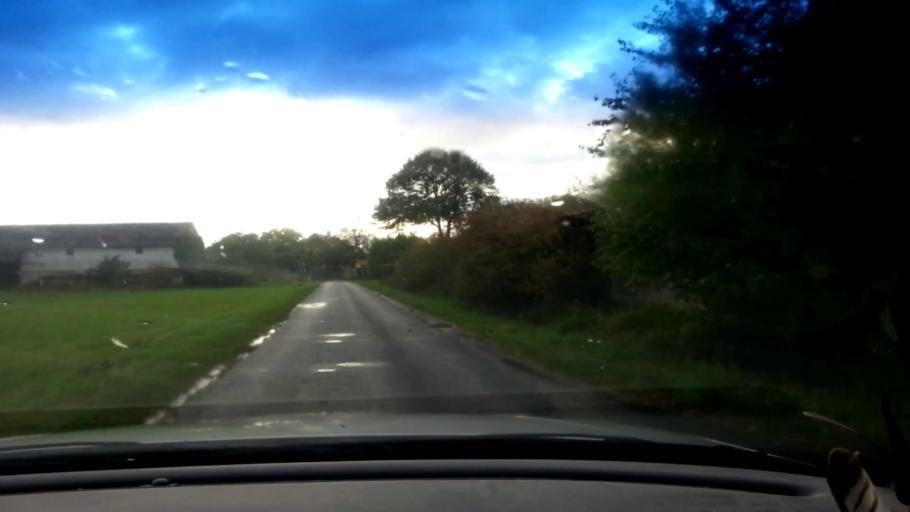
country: DE
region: Bavaria
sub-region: Upper Franconia
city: Burgebrach
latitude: 49.8272
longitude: 10.7074
